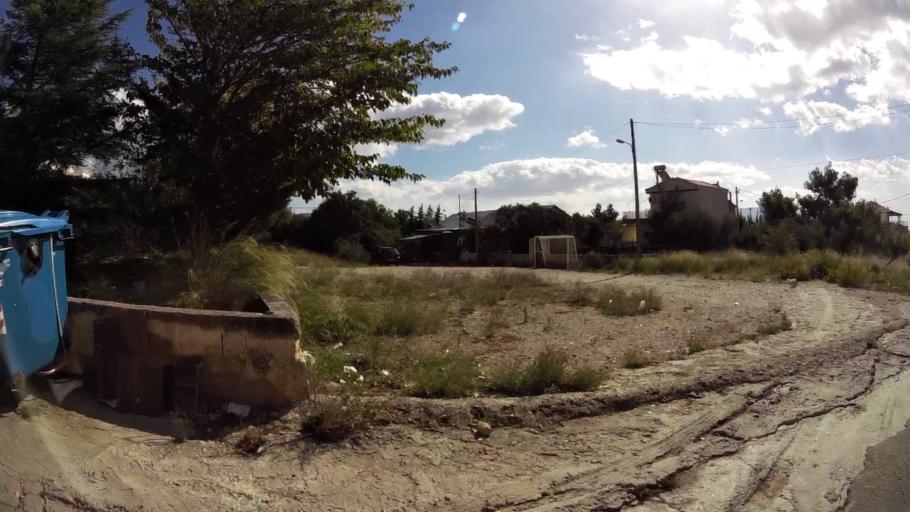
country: GR
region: Attica
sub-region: Nomarchia Anatolikis Attikis
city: Thrakomakedones
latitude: 38.1173
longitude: 23.7532
